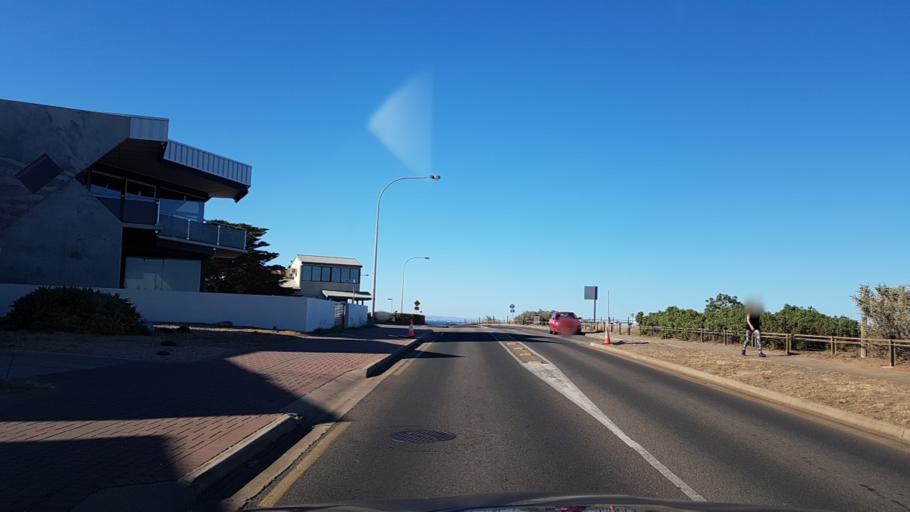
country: AU
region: South Australia
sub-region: Adelaide
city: Port Noarlunga
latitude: -35.1437
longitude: 138.4675
